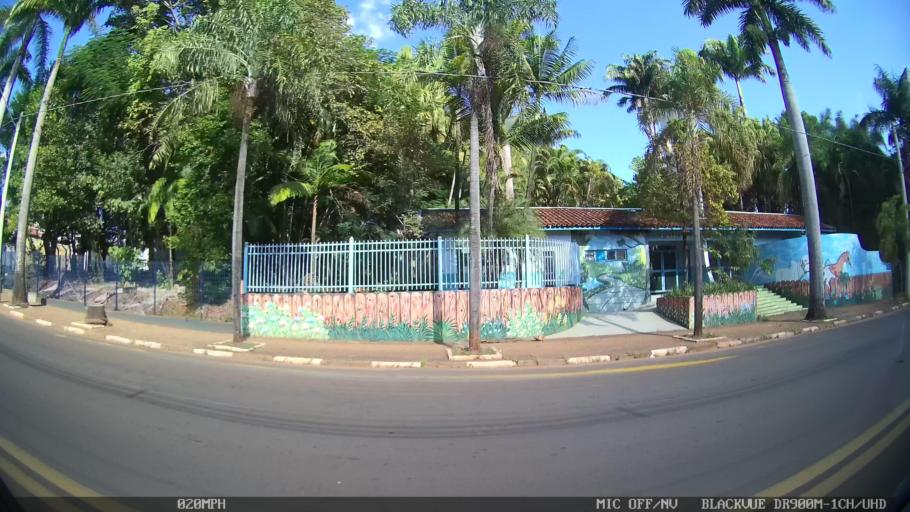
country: BR
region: Sao Paulo
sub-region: Sumare
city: Sumare
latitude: -22.8236
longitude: -47.2809
